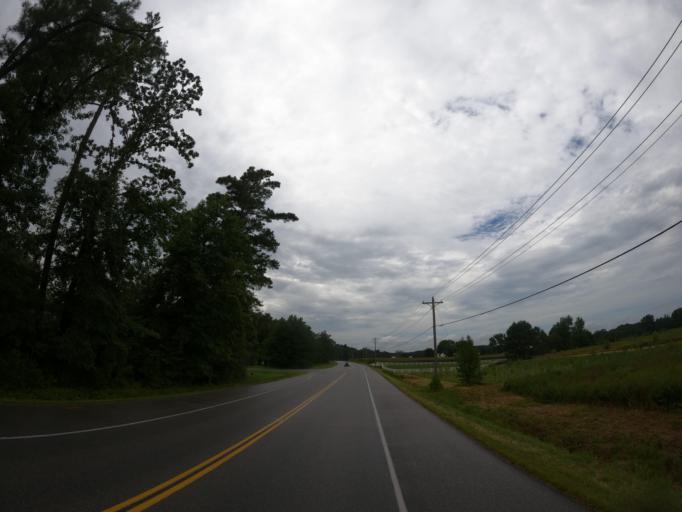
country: US
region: Maryland
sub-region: Saint Mary's County
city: California
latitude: 38.2761
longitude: -76.5407
